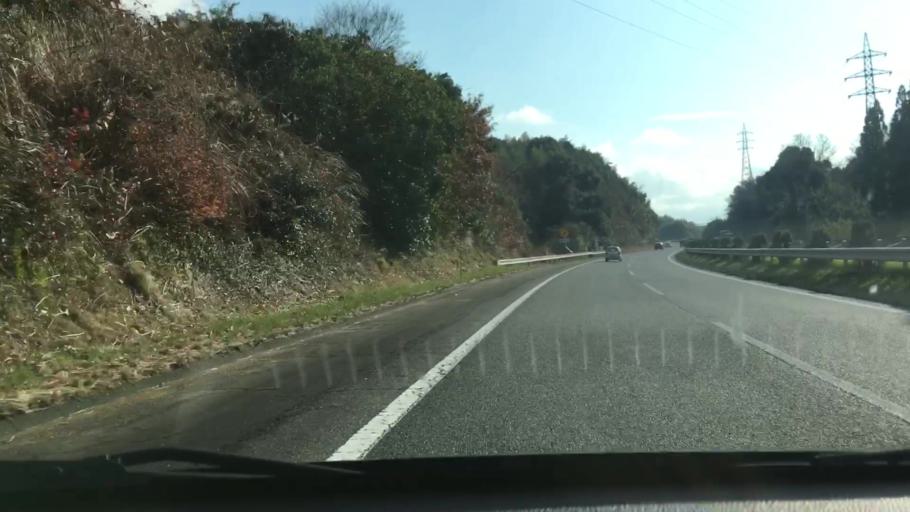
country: JP
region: Kumamoto
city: Matsubase
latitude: 32.6350
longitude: 130.7102
